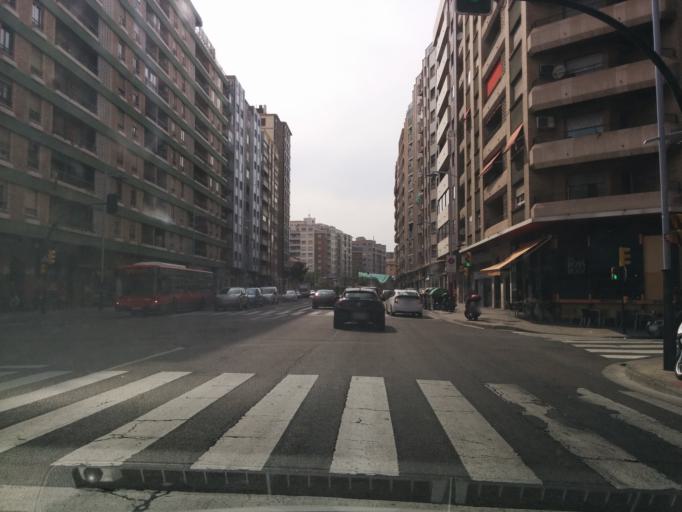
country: ES
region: Aragon
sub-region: Provincia de Zaragoza
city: Zaragoza
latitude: 41.6429
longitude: -0.8880
